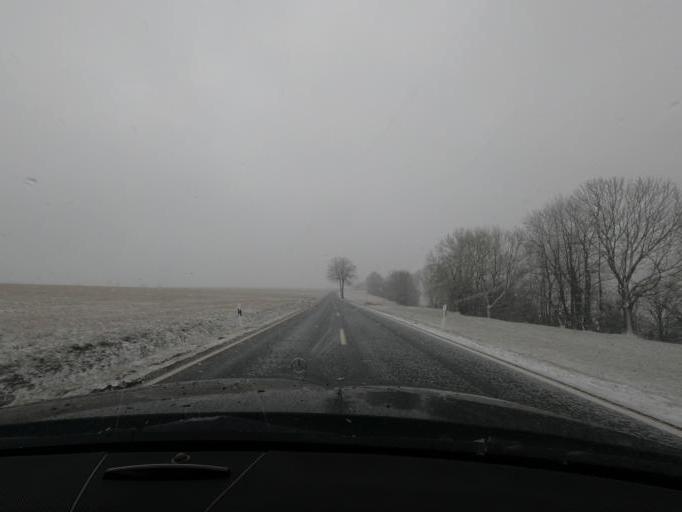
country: DE
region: Thuringia
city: Effelder
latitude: 51.2348
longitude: 10.2602
